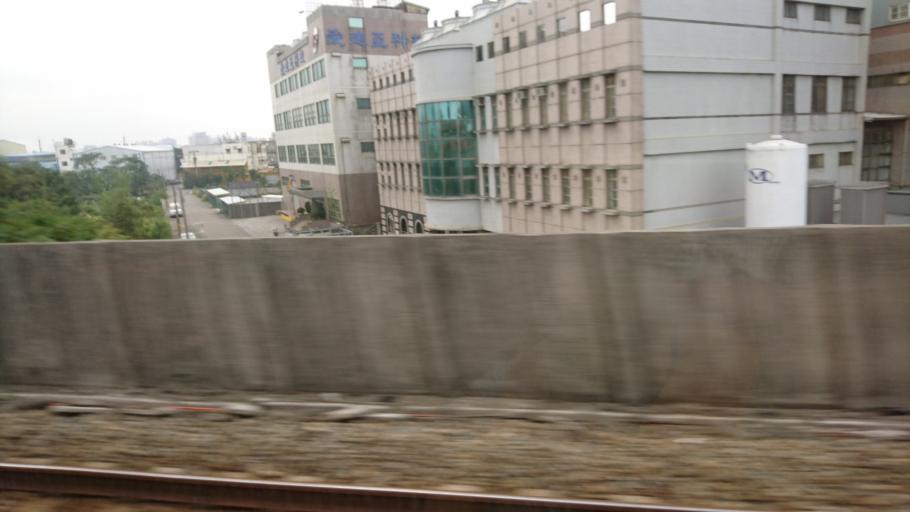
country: TW
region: Taiwan
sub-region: Hsinchu
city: Zhubei
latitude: 24.8486
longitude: 121.0138
